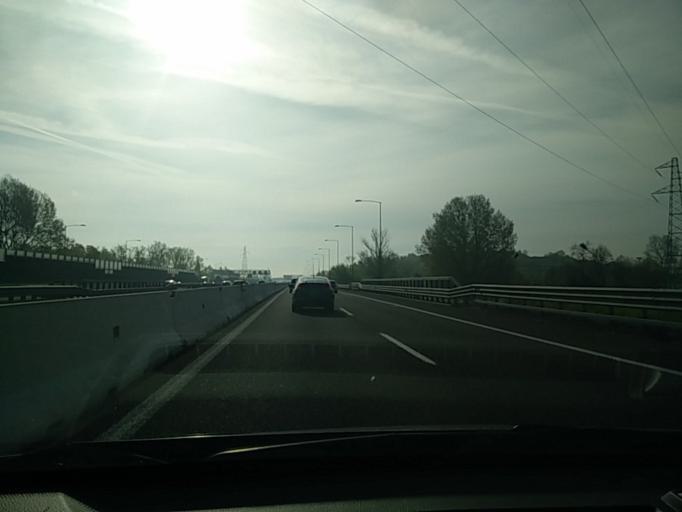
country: IT
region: Emilia-Romagna
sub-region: Provincia di Bologna
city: San Lazzaro
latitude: 44.4860
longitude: 11.4056
